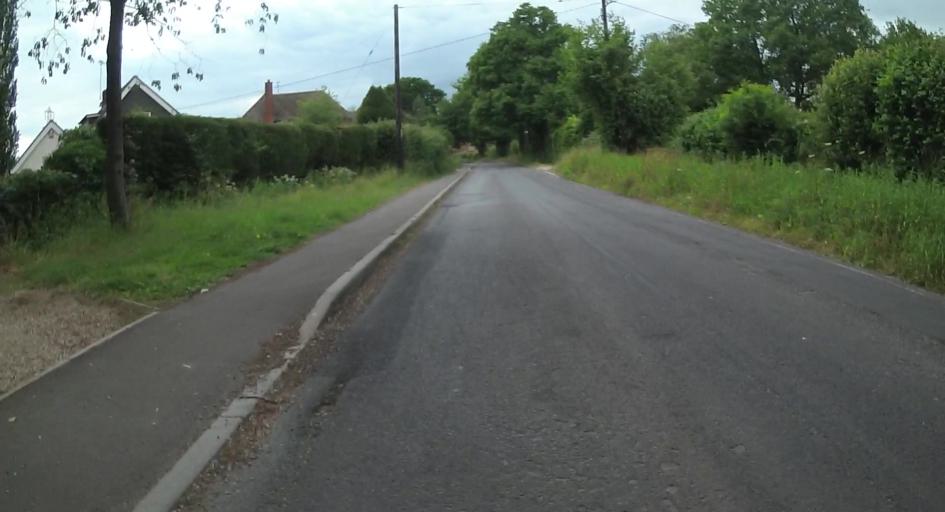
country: GB
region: England
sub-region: Hampshire
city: Fleet
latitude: 51.2685
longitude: -0.8677
